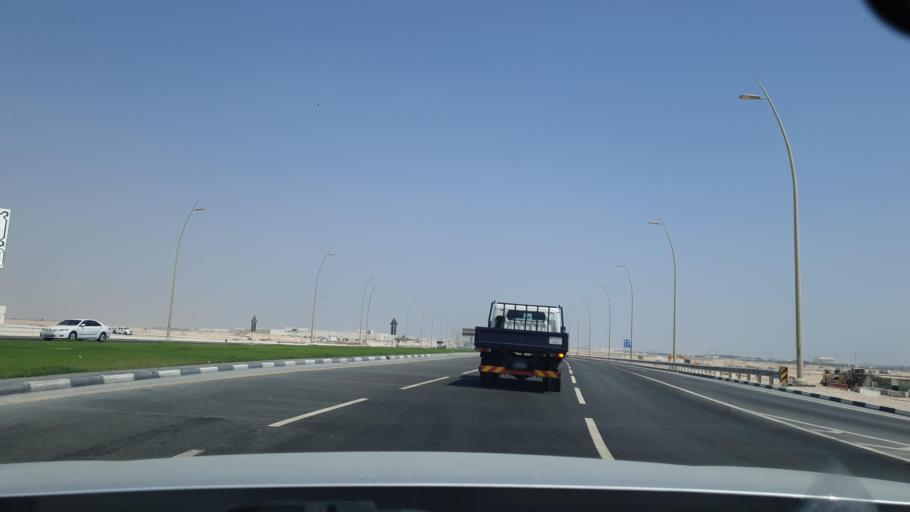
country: QA
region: Al Khawr
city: Al Khawr
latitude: 25.6513
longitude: 51.4567
